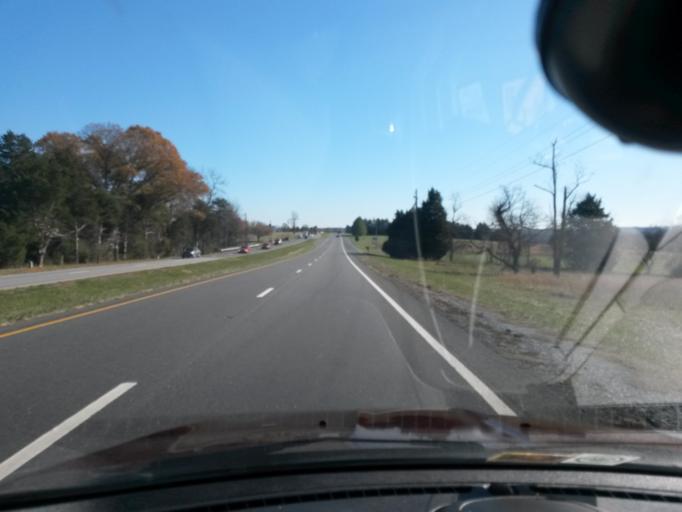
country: US
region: Virginia
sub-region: City of Bedford
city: Bedford
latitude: 37.3182
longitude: -79.4191
